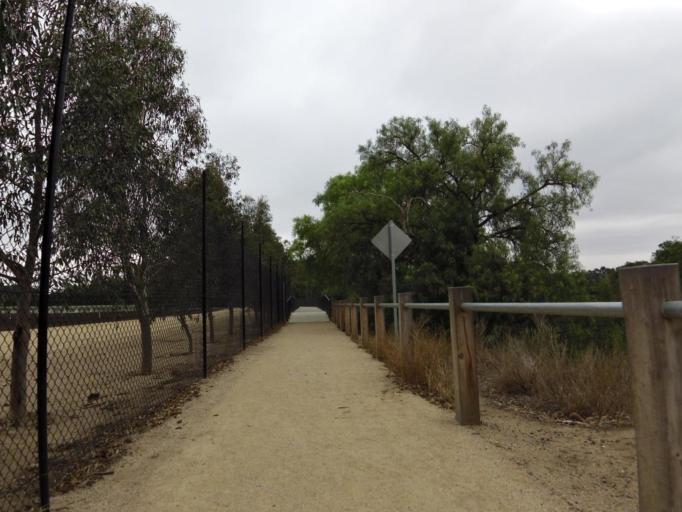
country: AU
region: Victoria
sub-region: Moorabool
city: Bacchus Marsh
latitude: -37.6589
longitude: 144.4504
